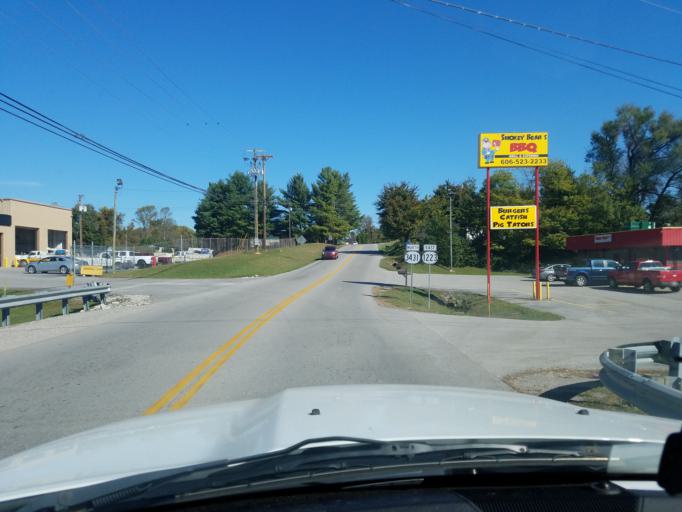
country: US
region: Kentucky
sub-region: Laurel County
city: North Corbin
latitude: 36.9725
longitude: -84.0919
